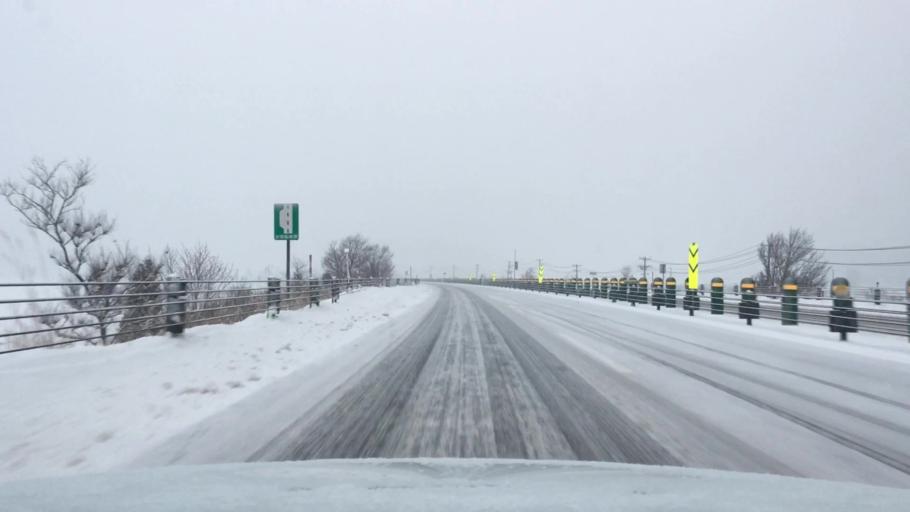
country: JP
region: Akita
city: Hanawa
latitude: 40.2912
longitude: 140.7575
